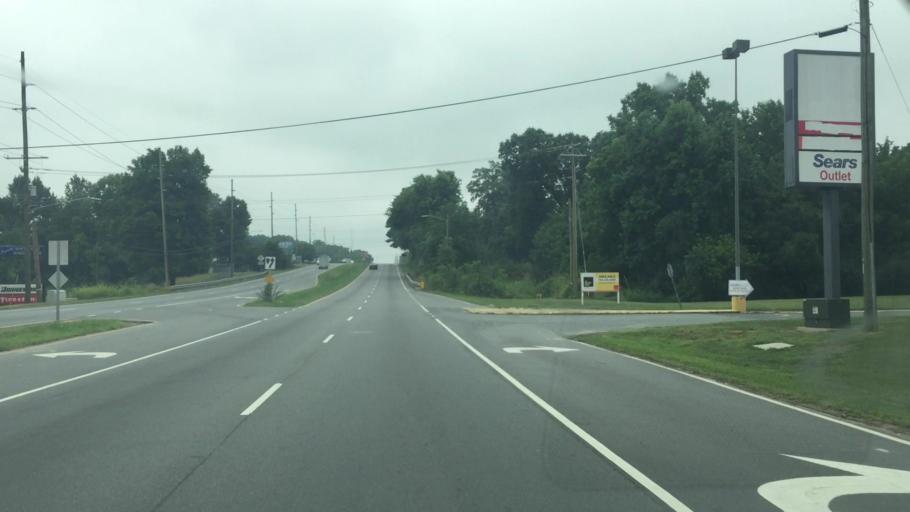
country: US
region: North Carolina
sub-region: Cabarrus County
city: Concord
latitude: 35.4132
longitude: -80.6129
